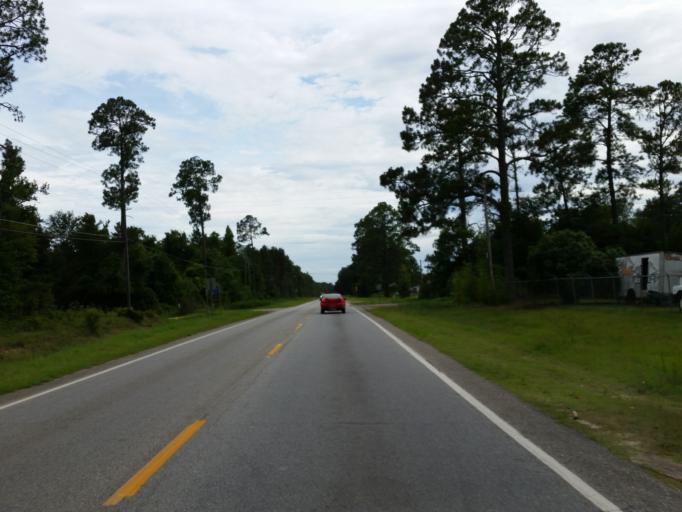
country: US
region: Georgia
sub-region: Lowndes County
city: Valdosta
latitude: 30.7422
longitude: -83.2781
